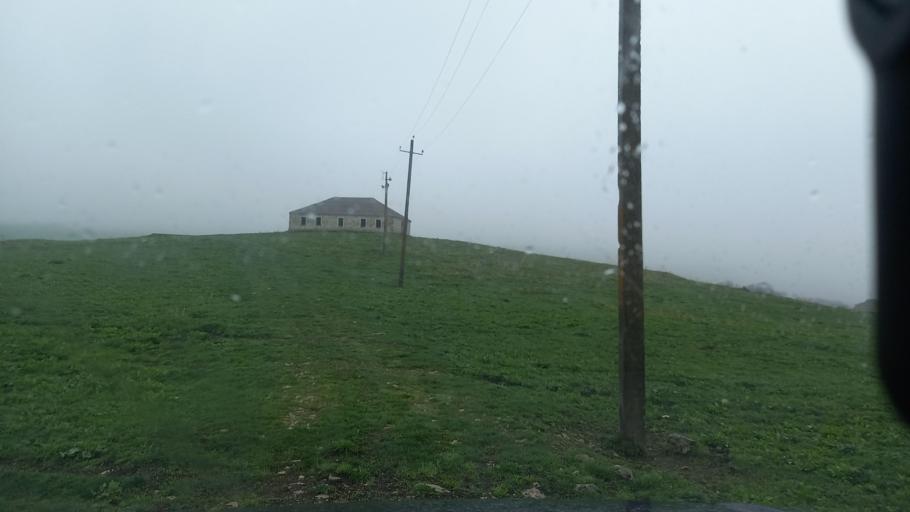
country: RU
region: Kabardino-Balkariya
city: Kamennomostskoye
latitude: 43.6459
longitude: 42.9824
